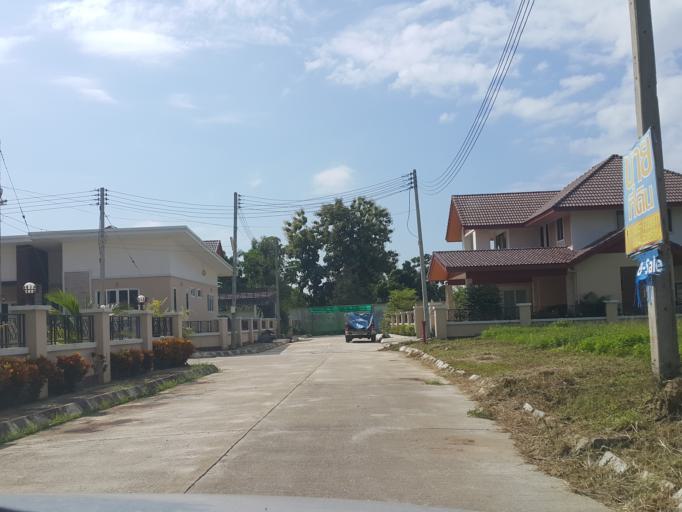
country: TH
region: Chiang Mai
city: Saraphi
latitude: 18.7371
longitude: 99.0452
